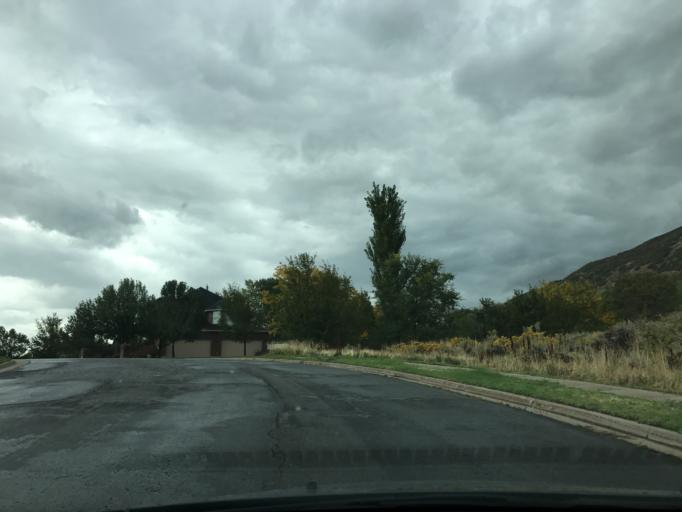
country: US
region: Utah
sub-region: Davis County
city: Fruit Heights
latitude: 41.0208
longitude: -111.8993
